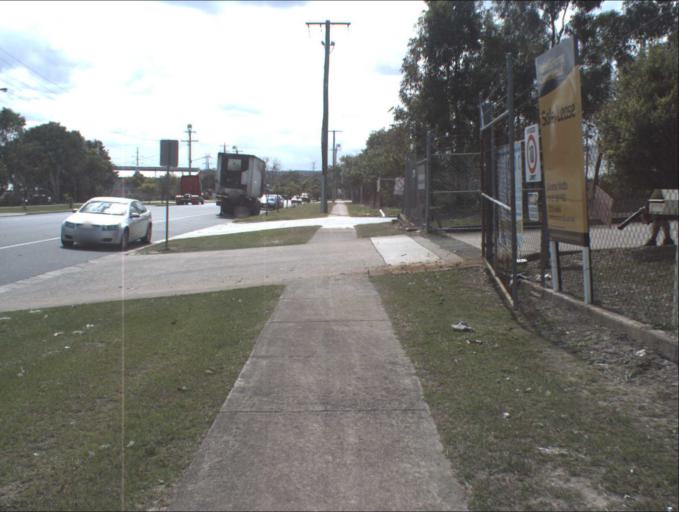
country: AU
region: Queensland
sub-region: Logan
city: Logan Reserve
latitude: -27.6831
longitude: 153.0706
